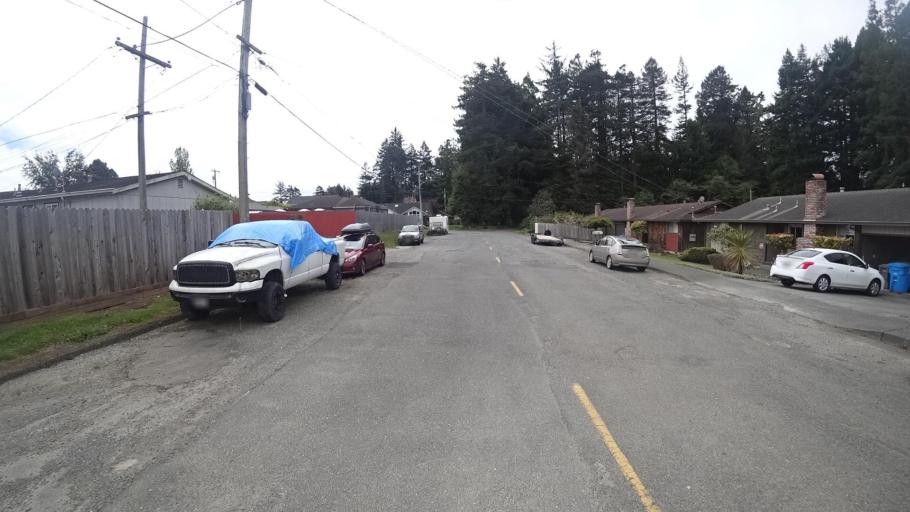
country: US
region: California
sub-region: Humboldt County
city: Cutten
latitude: 40.7704
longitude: -124.1477
